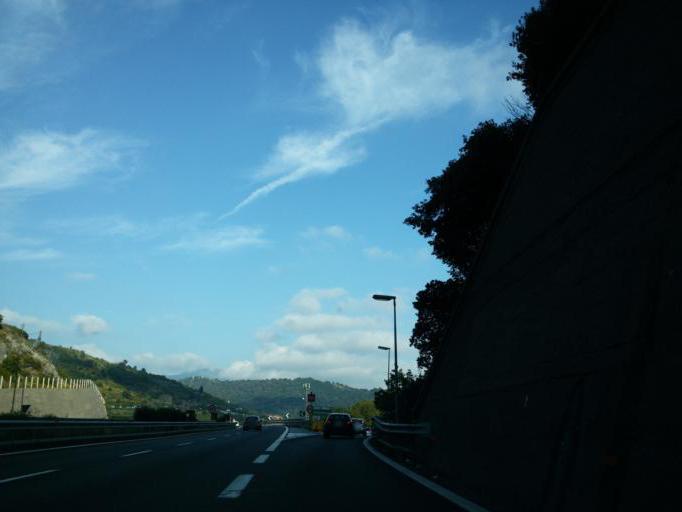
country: IT
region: Liguria
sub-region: Provincia di Genova
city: Genoa
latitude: 44.4377
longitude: 8.9396
